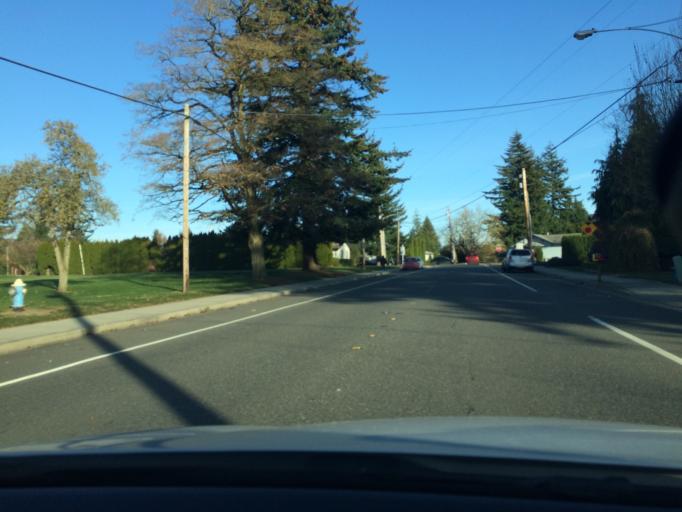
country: US
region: Washington
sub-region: Whatcom County
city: Lynden
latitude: 48.9493
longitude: -122.4426
